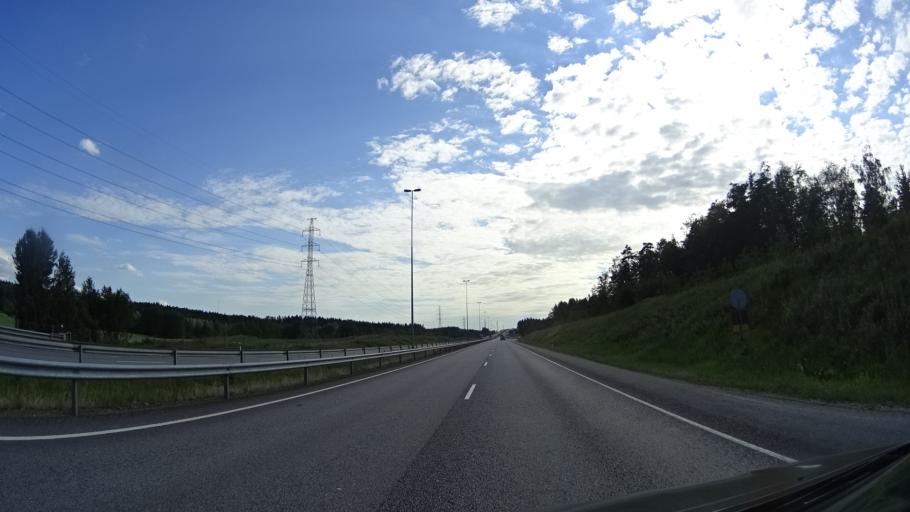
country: FI
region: South Karelia
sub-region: Lappeenranta
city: Lappeenranta
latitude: 61.0771
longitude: 28.3260
